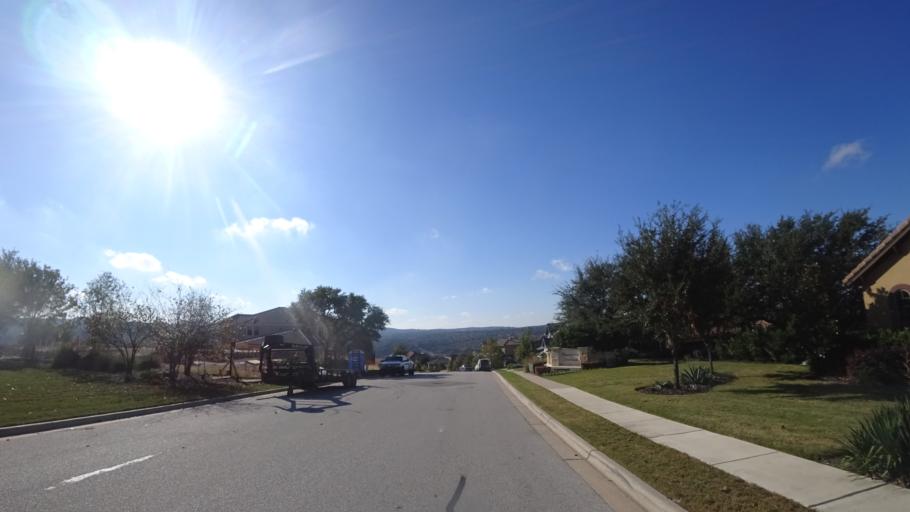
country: US
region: Texas
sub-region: Travis County
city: Bee Cave
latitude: 30.3463
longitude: -97.8940
